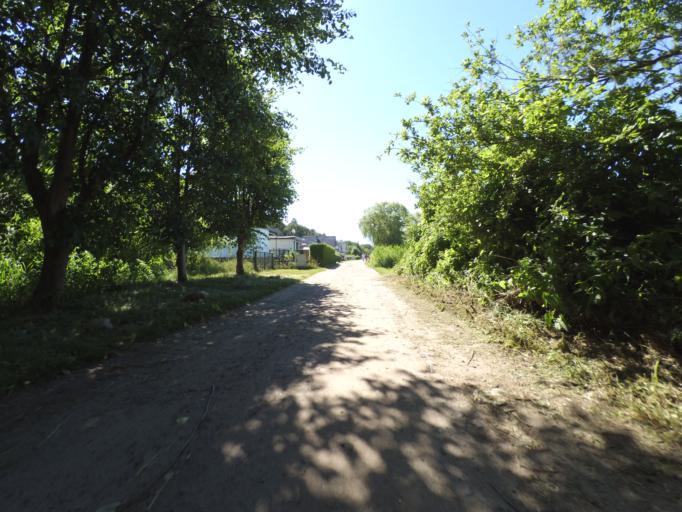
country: DE
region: Mecklenburg-Vorpommern
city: Plau am See
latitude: 53.5166
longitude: 12.3284
